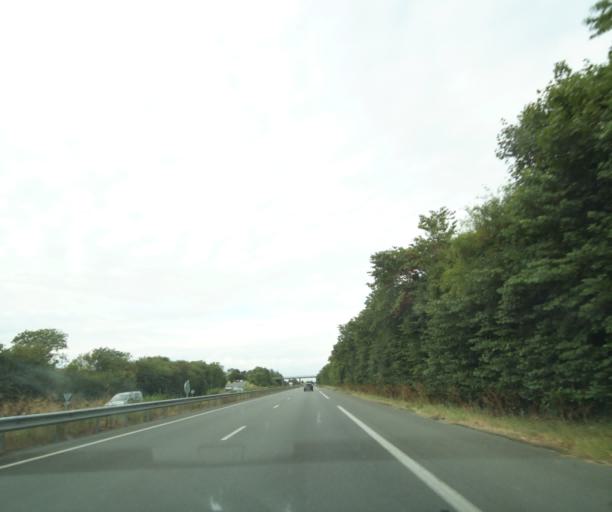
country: FR
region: Poitou-Charentes
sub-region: Departement de la Charente-Maritime
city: Dompierre-sur-Mer
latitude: 46.1880
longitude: -1.0739
